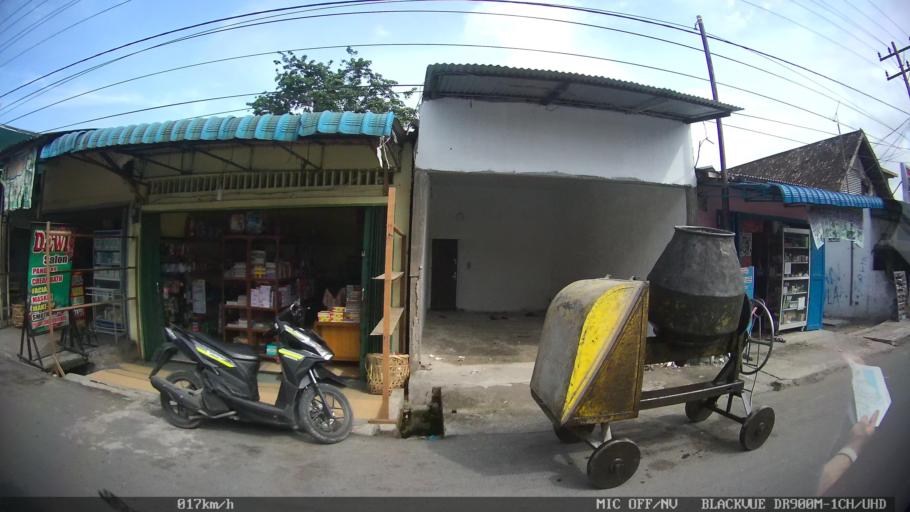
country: ID
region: North Sumatra
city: Medan
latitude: 3.5986
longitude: 98.7558
